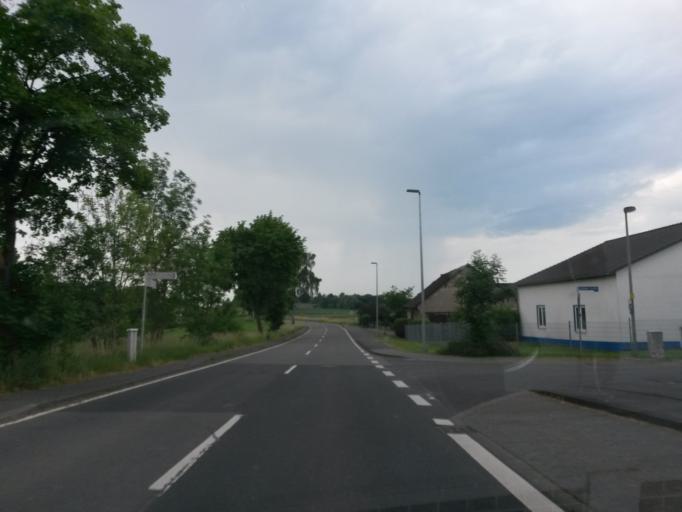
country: DE
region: North Rhine-Westphalia
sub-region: Regierungsbezirk Koln
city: Rosrath
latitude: 50.8929
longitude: 7.2369
